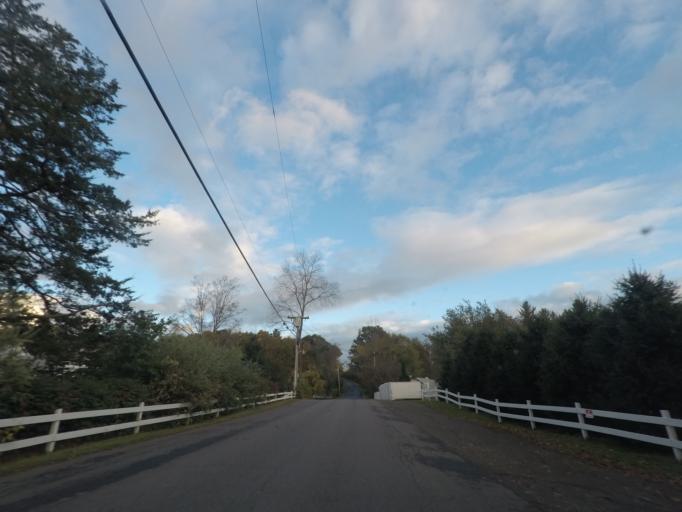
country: US
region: New York
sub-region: Rensselaer County
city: Nassau
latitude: 42.5510
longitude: -73.5896
